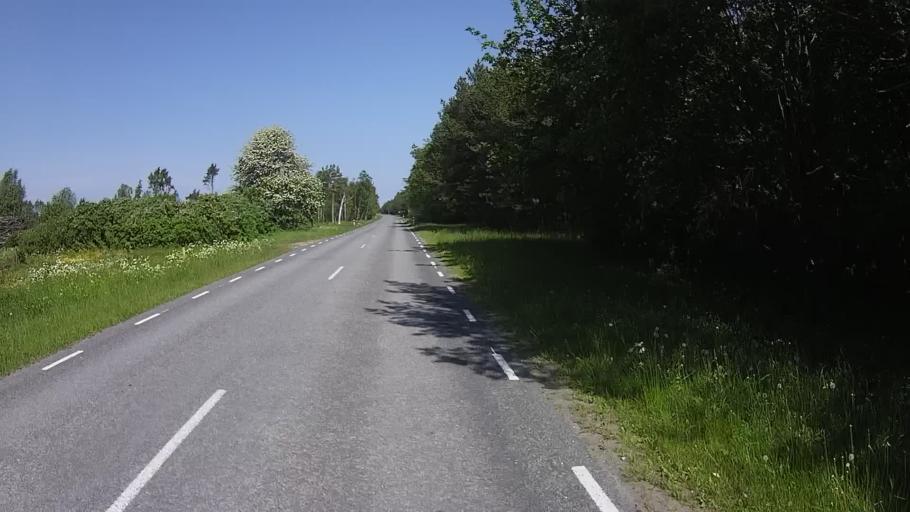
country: EE
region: Saare
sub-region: Kuressaare linn
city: Kuressaare
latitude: 58.1363
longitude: 22.2477
